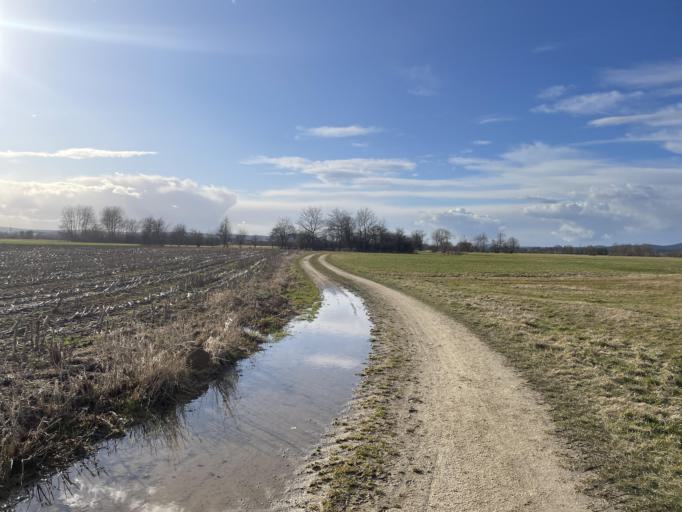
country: DE
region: Bavaria
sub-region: Upper Palatinate
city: Cham
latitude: 49.2173
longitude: 12.6580
